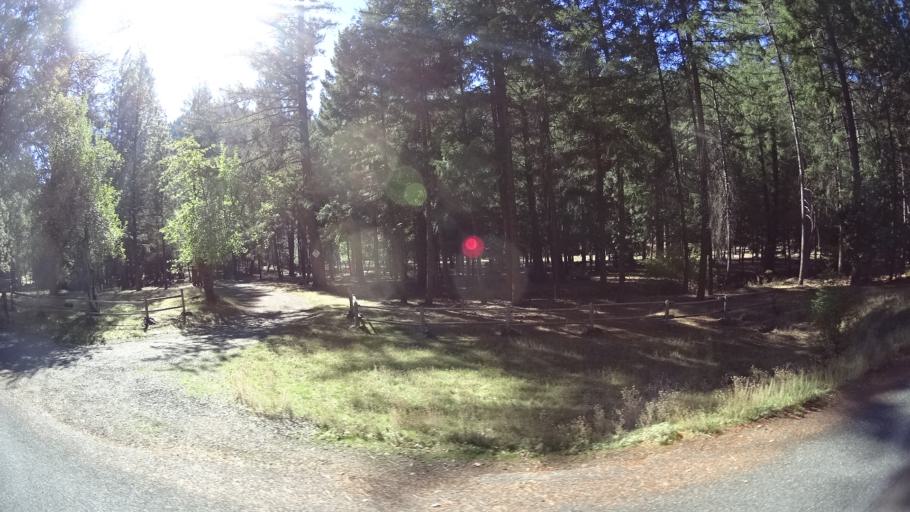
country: US
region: California
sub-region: Trinity County
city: Weaverville
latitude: 41.1435
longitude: -123.1565
